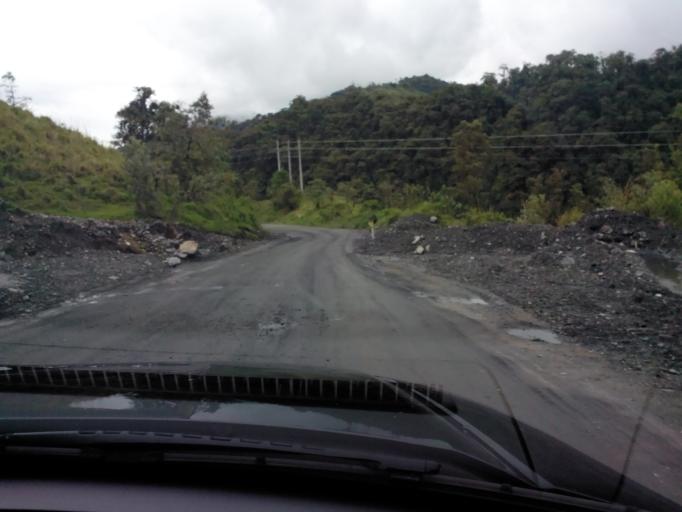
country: EC
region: Napo
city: Archidona
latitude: -0.5109
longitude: -77.8799
